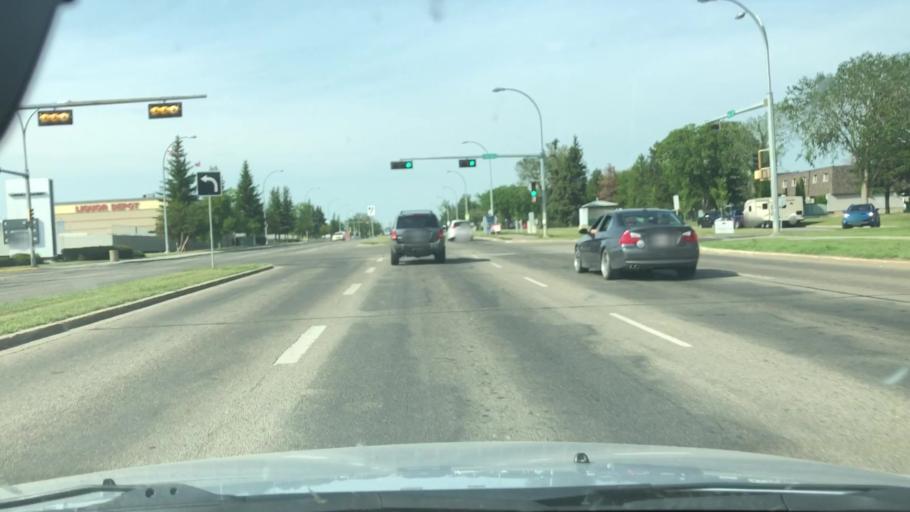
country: CA
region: Alberta
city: Edmonton
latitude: 53.6015
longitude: -113.4428
